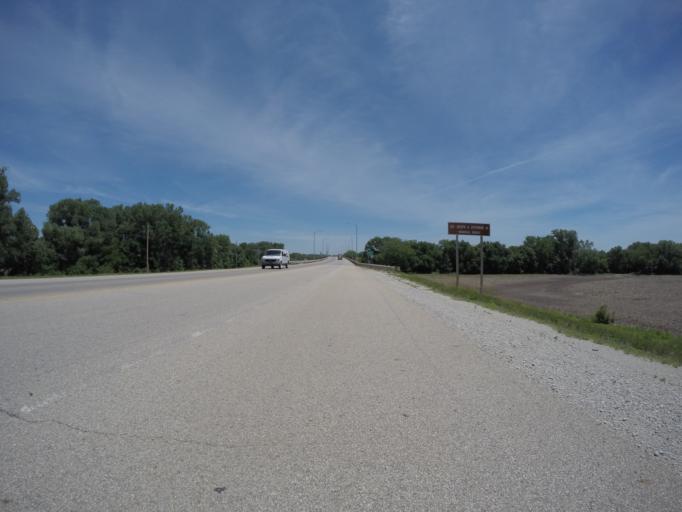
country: US
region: Kansas
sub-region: Marshall County
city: Marysville
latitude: 39.8421
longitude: -96.6637
